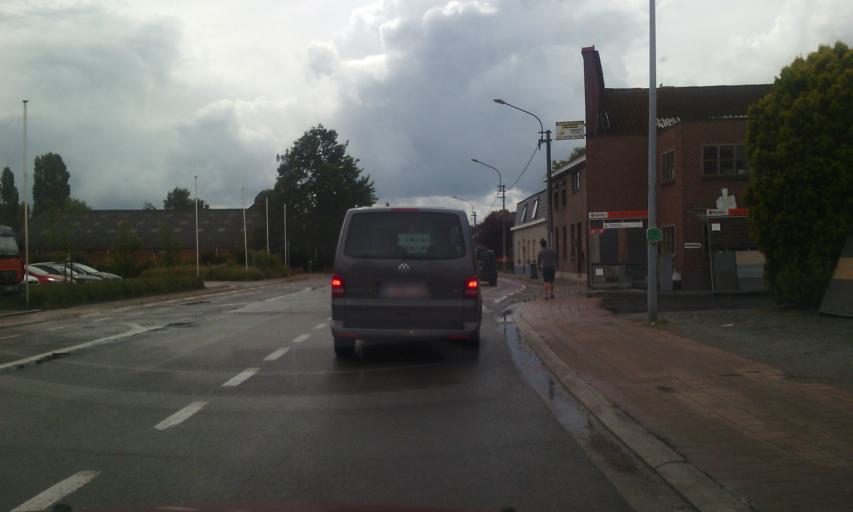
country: BE
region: Flanders
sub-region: Provincie Oost-Vlaanderen
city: Wetteren
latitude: 51.0336
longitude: 3.9115
